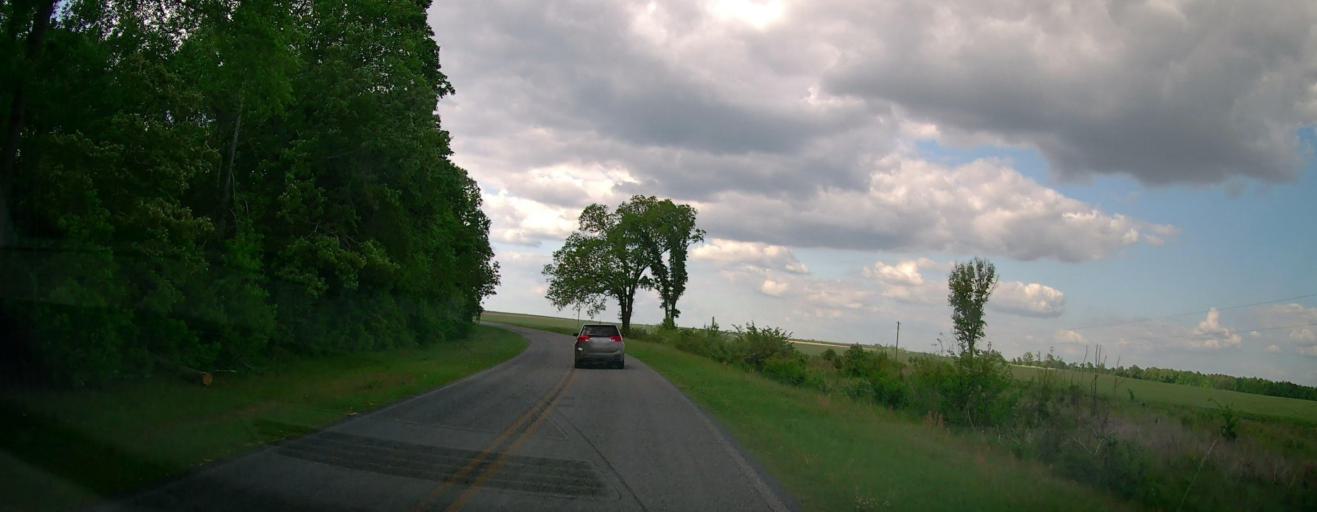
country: US
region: Georgia
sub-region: Laurens County
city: East Dublin
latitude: 32.6813
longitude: -82.8922
